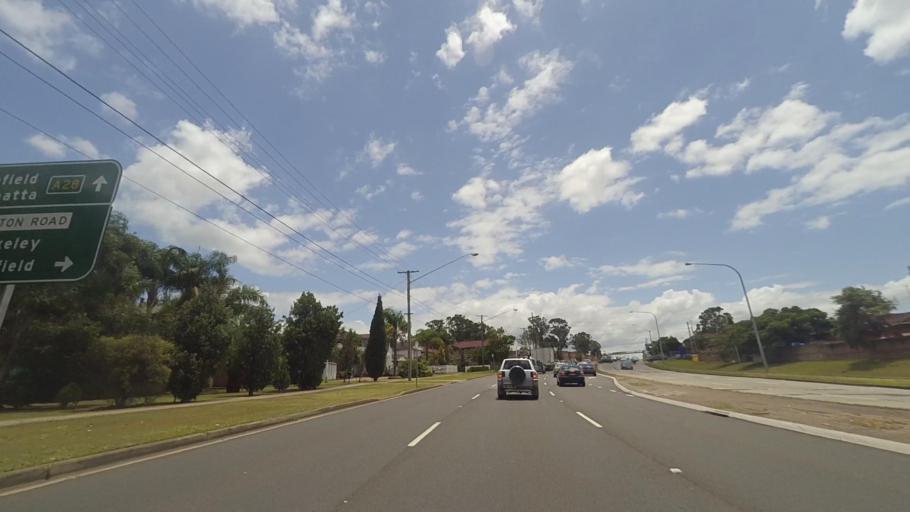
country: AU
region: New South Wales
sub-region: Fairfield
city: Fairfield Heights
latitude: -33.8708
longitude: 150.9251
